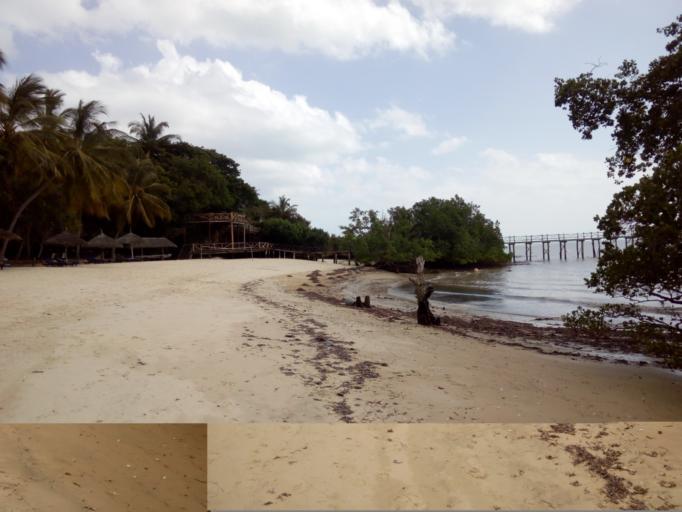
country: TZ
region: Zanzibar Urban/West
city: Zanzibar
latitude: -6.2100
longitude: 39.2014
